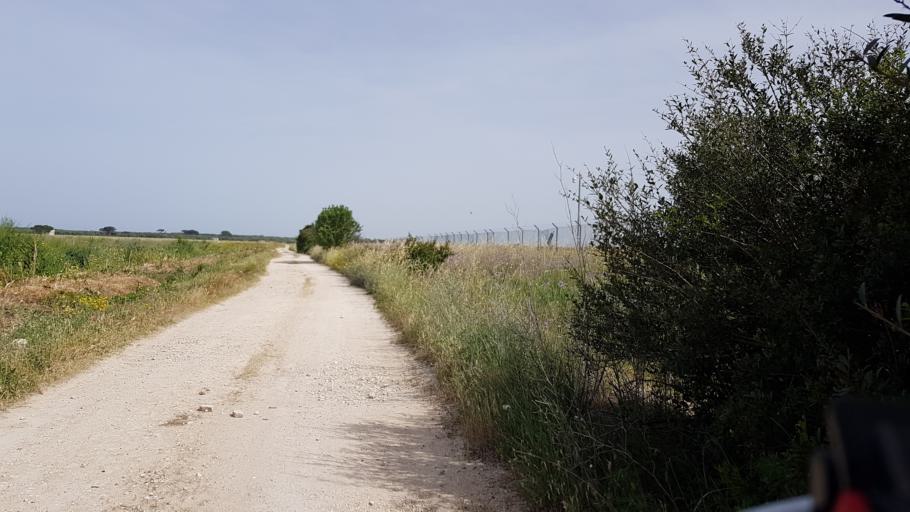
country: IT
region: Apulia
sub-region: Provincia di Brindisi
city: La Rosa
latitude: 40.5956
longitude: 17.9927
